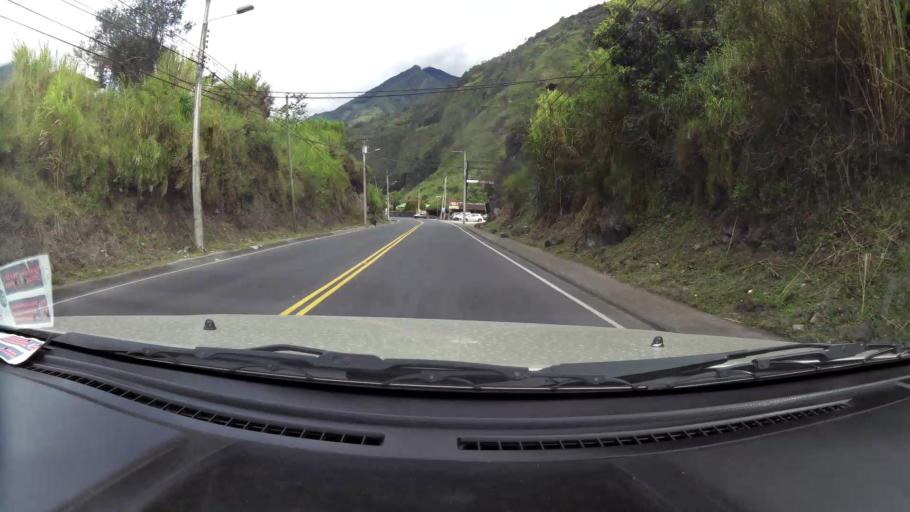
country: EC
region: Tungurahua
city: Banos
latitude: -1.3933
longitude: -78.4134
